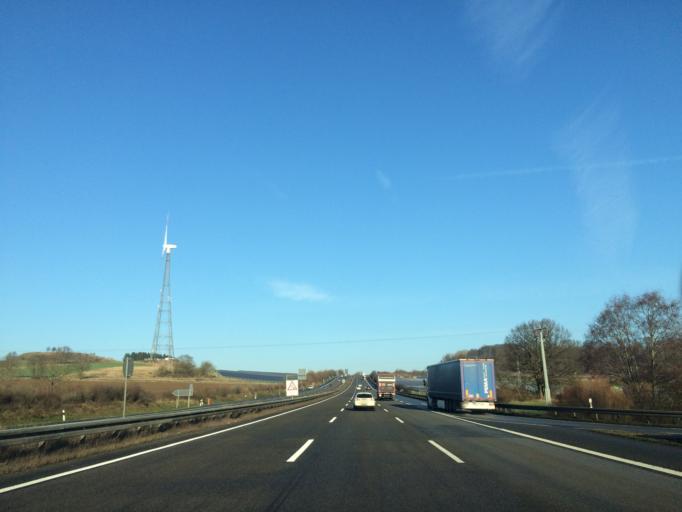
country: DE
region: Hesse
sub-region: Regierungsbezirk Kassel
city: Malsfeld
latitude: 51.0888
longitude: 9.4842
